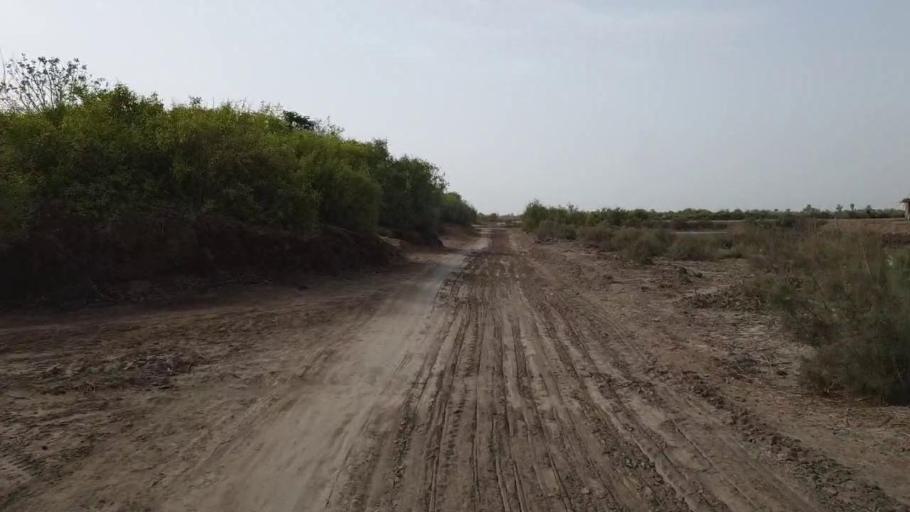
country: PK
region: Sindh
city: Daur
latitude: 26.4250
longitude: 68.1585
